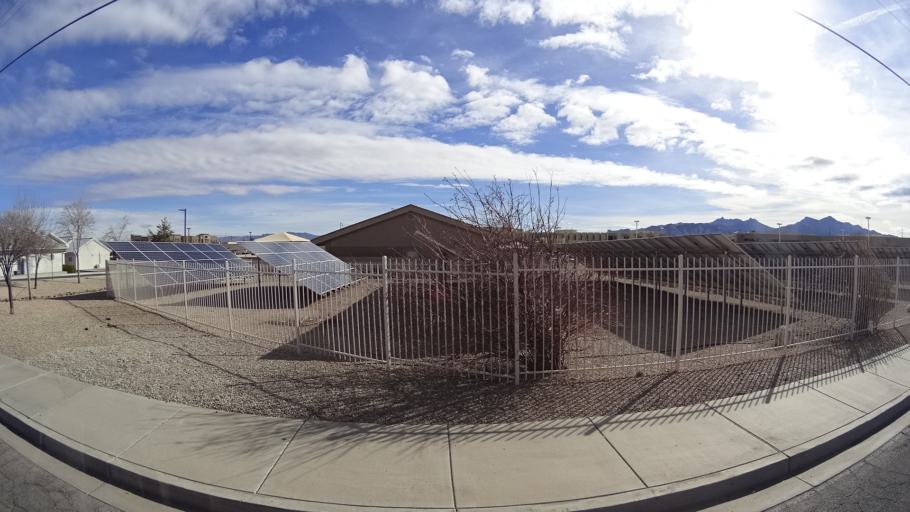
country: US
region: Arizona
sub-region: Mohave County
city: Kingman
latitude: 35.2208
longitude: -114.0401
